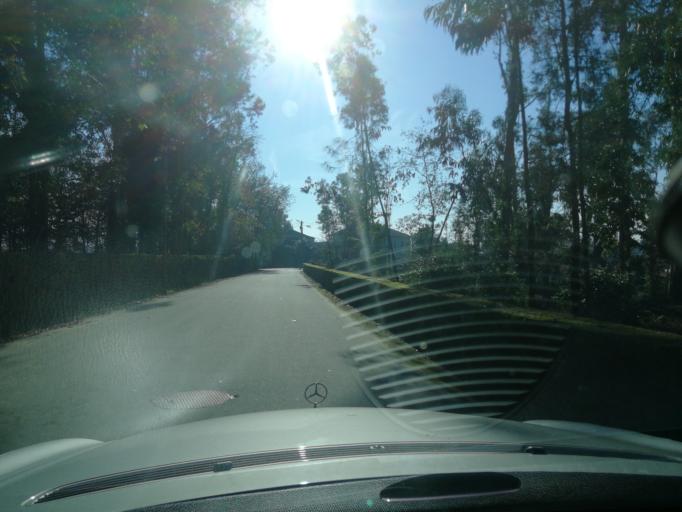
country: PT
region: Braga
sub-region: Braga
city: Adaufe
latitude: 41.6148
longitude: -8.3978
